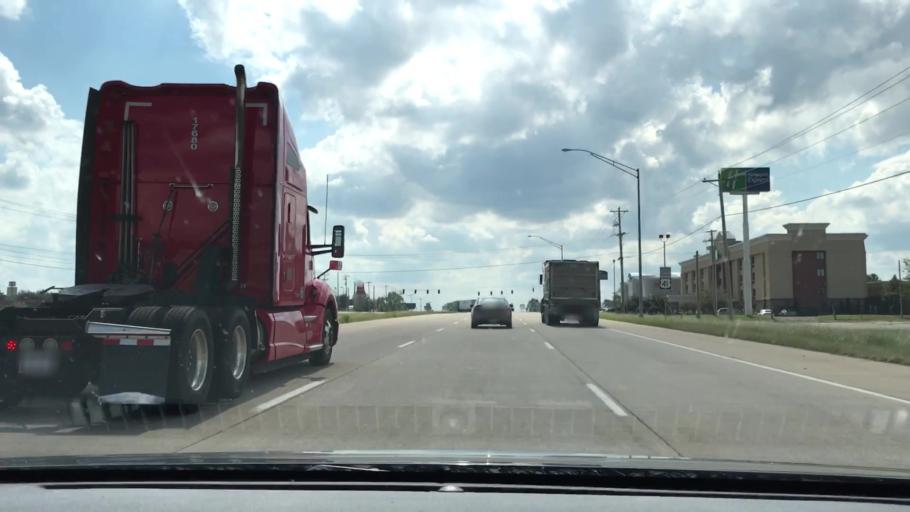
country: US
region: Kentucky
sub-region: Christian County
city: Oak Grove
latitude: 36.6955
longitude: -87.4533
